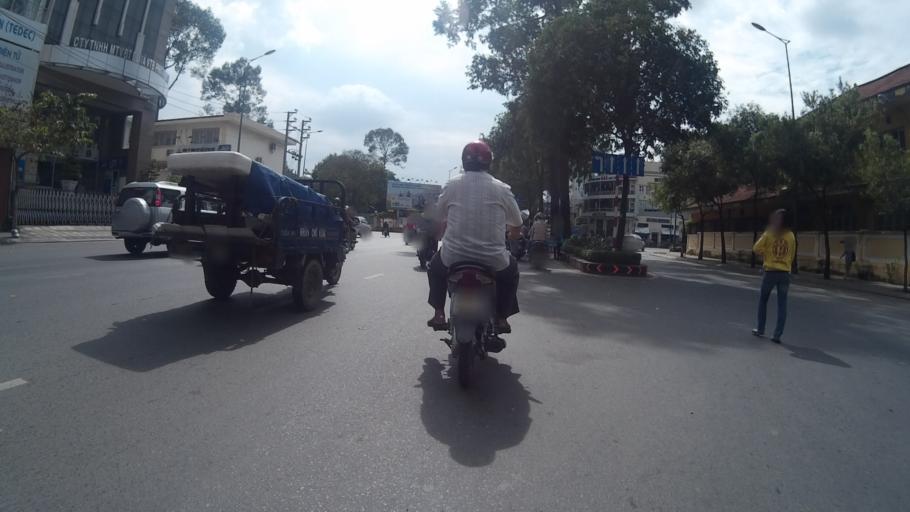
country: VN
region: Ho Chi Minh City
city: Quan Ba
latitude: 10.7854
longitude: 106.6895
